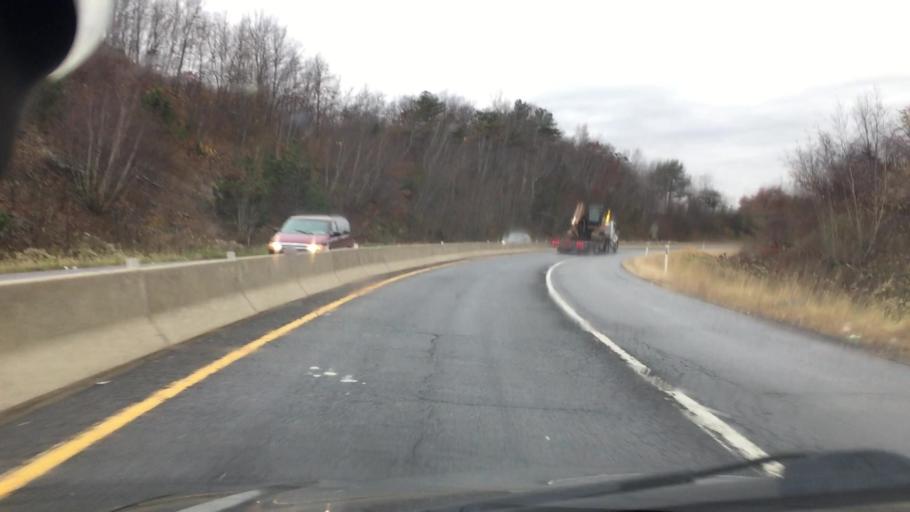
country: US
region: Pennsylvania
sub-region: Luzerne County
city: Ashley
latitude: 41.2019
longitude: -75.9032
